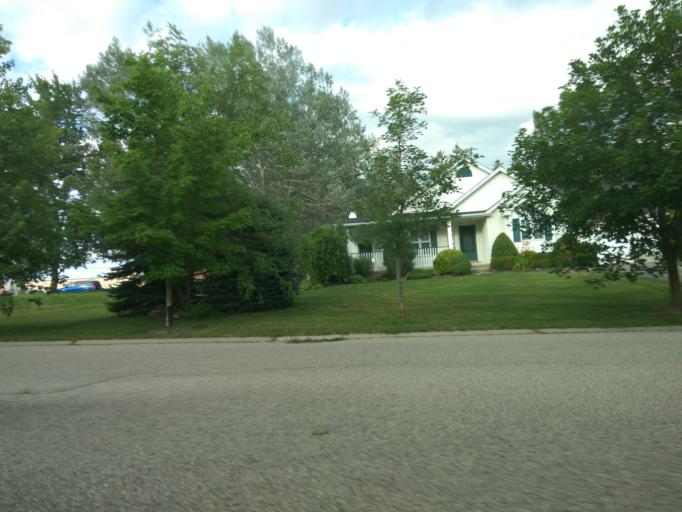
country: CA
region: Ontario
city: Kitchener
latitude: 43.3744
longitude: -80.6990
